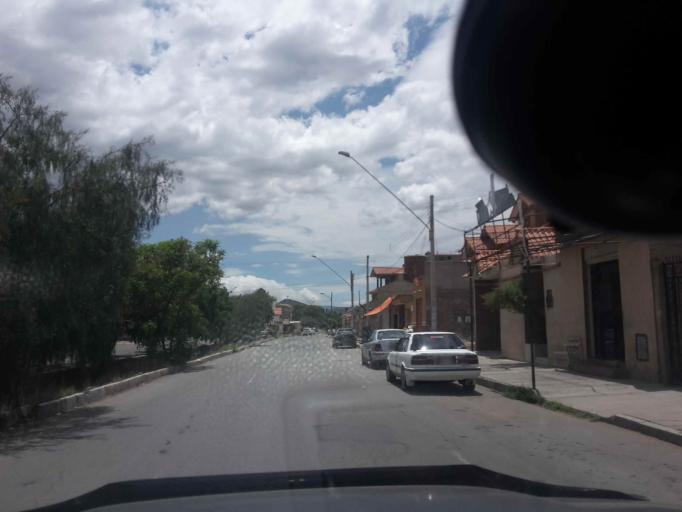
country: BO
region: Cochabamba
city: Cochabamba
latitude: -17.3817
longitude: -66.1959
